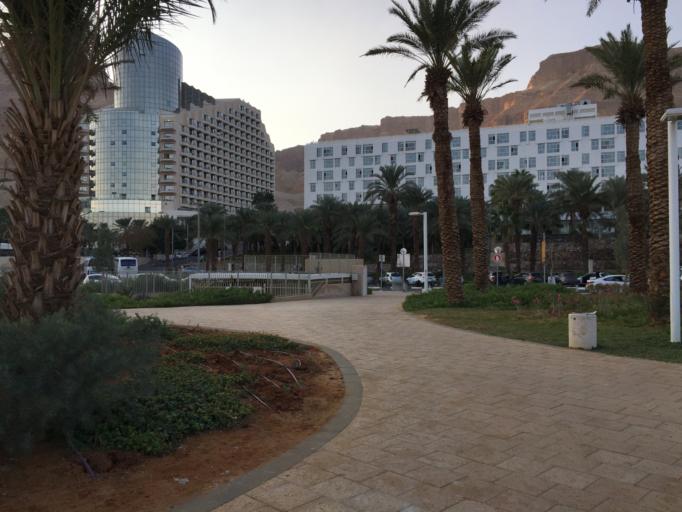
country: IL
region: Southern District
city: `En Boqeq
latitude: 31.1971
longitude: 35.3632
